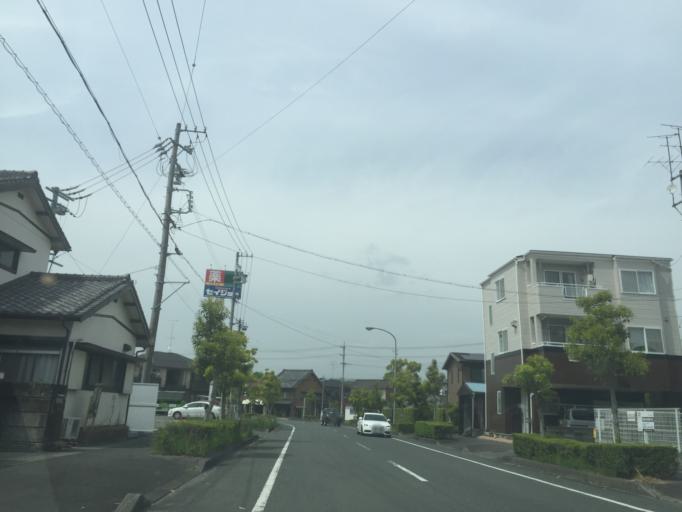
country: JP
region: Shizuoka
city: Kakegawa
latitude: 34.7737
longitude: 138.0031
